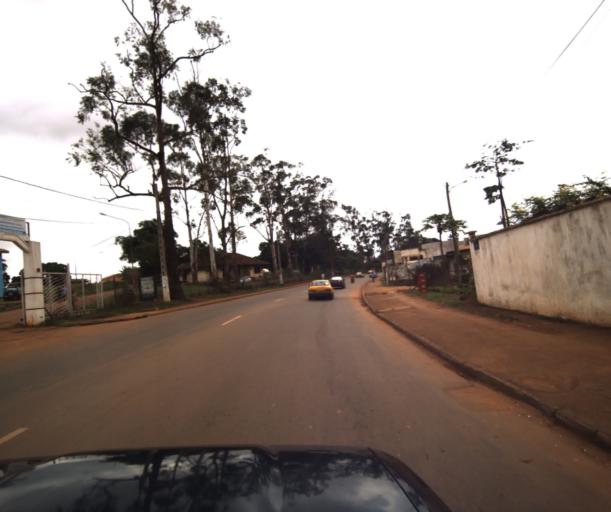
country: CM
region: Centre
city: Yaounde
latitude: 3.8368
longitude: 11.5181
